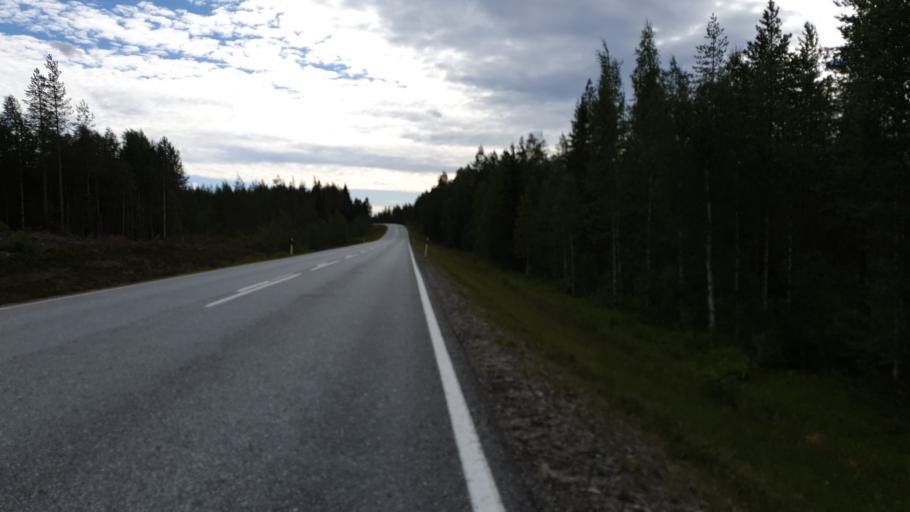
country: FI
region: Kainuu
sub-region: Kehys-Kainuu
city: Kuhmo
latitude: 64.4802
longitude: 29.7525
